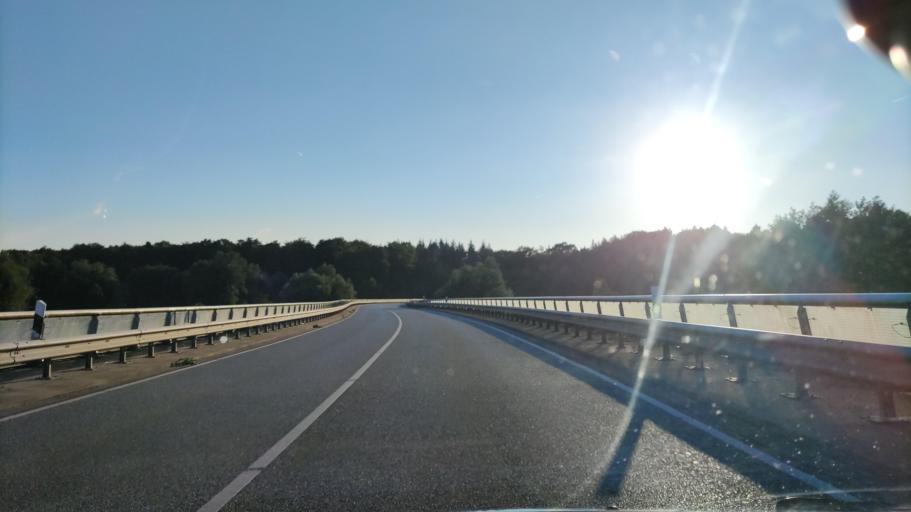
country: DE
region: Schleswig-Holstein
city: Preetz
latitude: 54.2488
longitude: 10.2871
